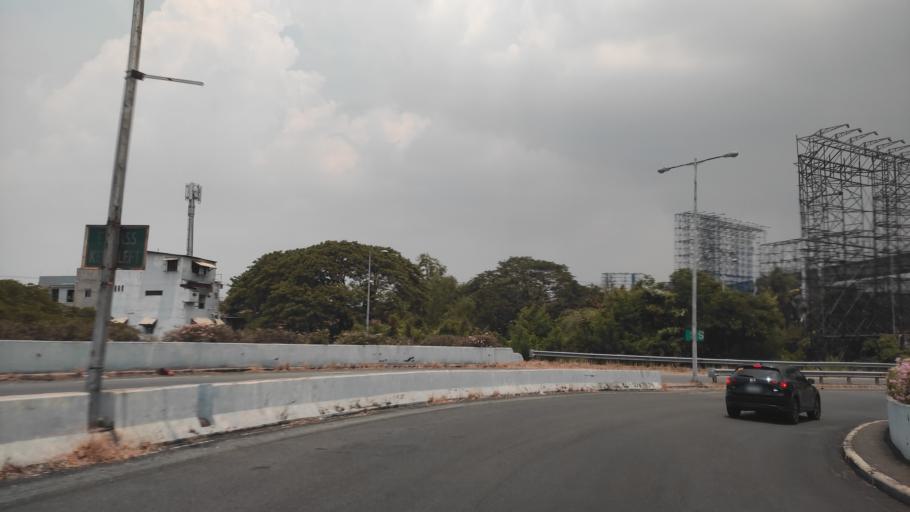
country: PH
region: Calabarzon
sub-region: Province of Laguna
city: San Pedro
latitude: 14.4101
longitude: 121.0435
